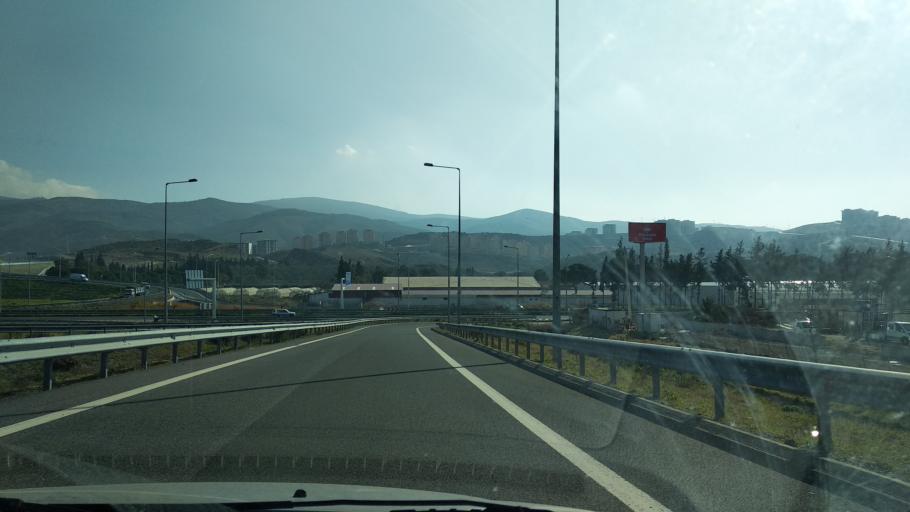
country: TR
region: Izmir
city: Menemen
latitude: 38.5705
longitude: 27.0543
